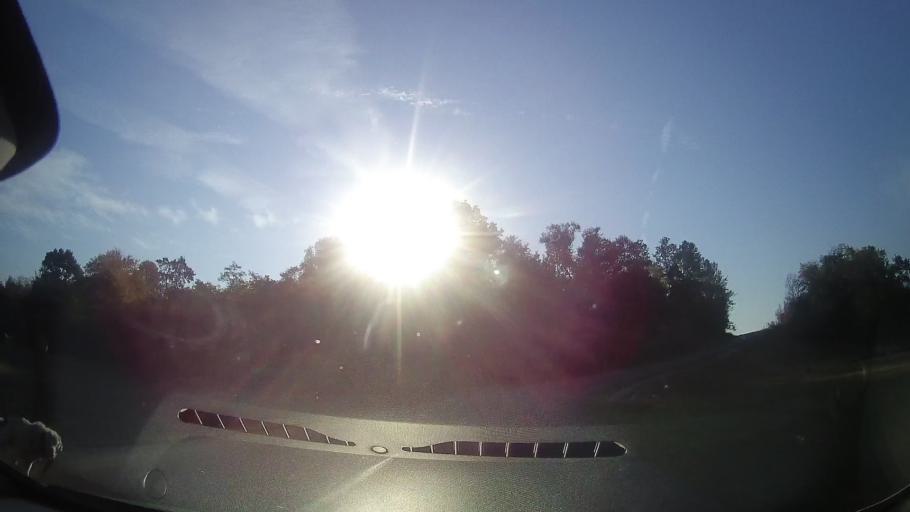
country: RO
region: Timis
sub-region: Comuna Bogda
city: Bogda
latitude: 45.9734
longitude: 21.6013
